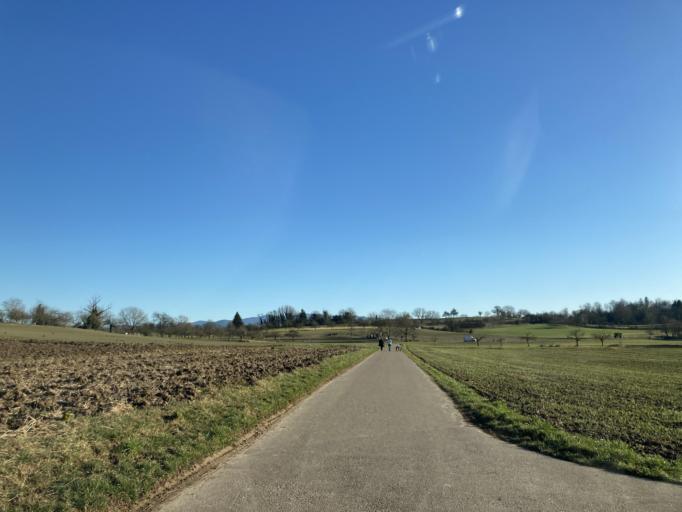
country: DE
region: Baden-Wuerttemberg
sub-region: Freiburg Region
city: Umkirch
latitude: 48.0593
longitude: 7.7888
